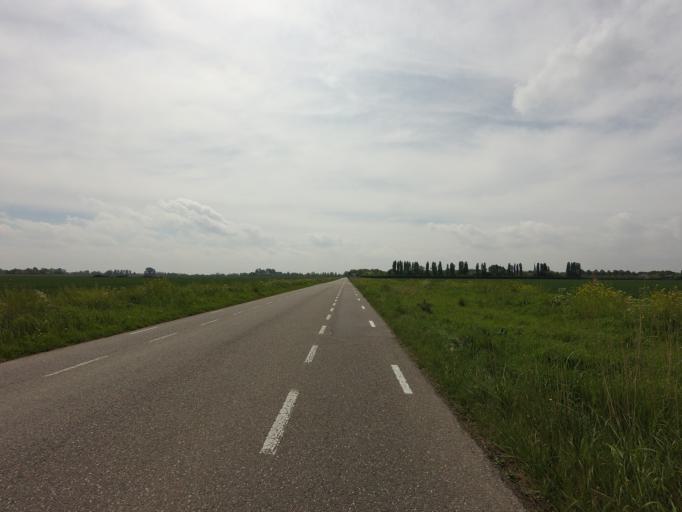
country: NL
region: South Holland
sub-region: Gemeente Binnenmaas
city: Mijnsheerenland
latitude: 51.8027
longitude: 4.5036
